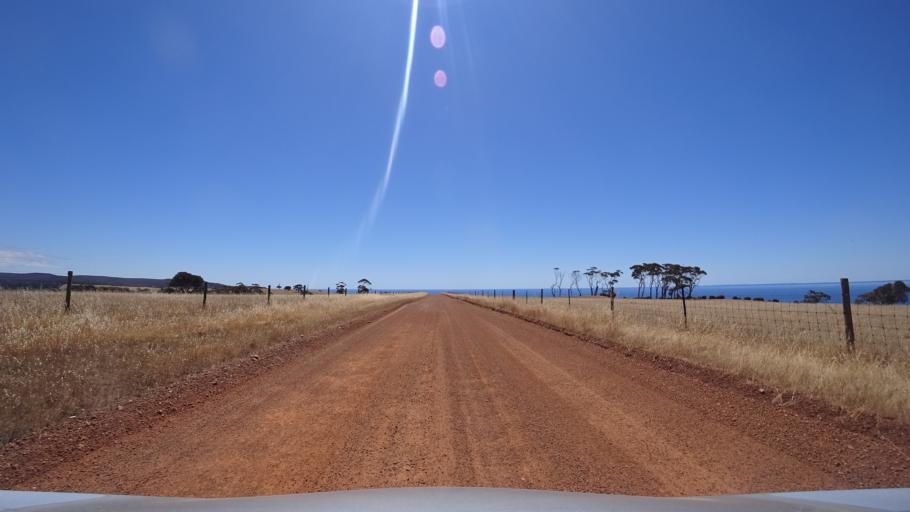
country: AU
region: South Australia
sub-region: Kangaroo Island
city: Kingscote
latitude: -35.6803
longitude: 136.9925
